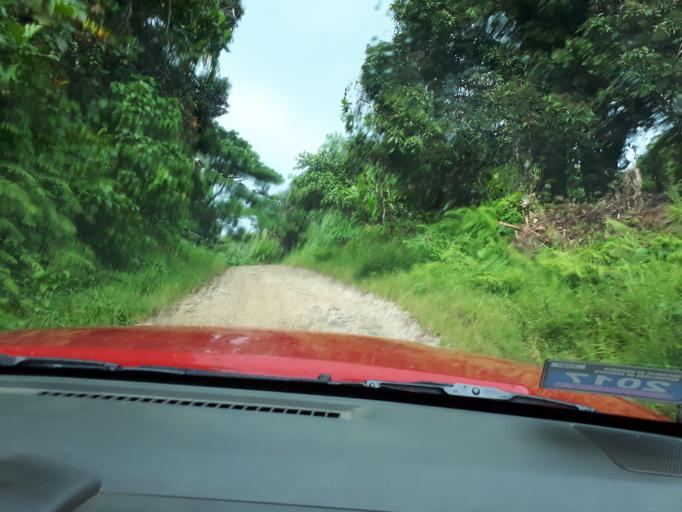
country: VU
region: Sanma
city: Luganville
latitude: -15.5703
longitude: 166.9468
